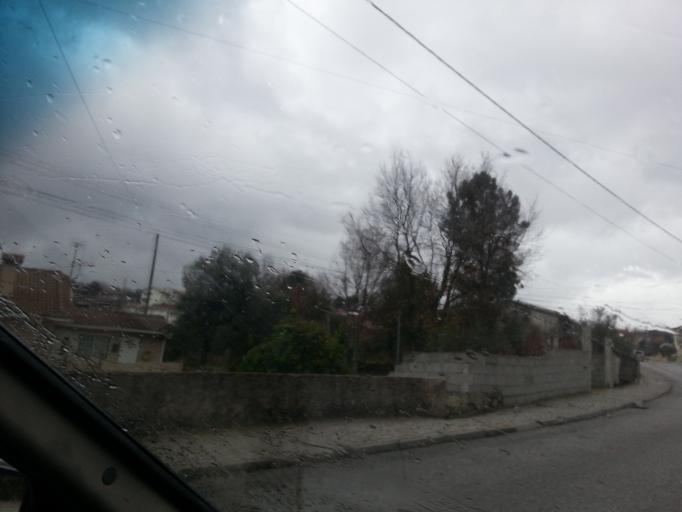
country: PT
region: Viseu
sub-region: Viseu
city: Rio de Loba
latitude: 40.6667
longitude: -7.8787
